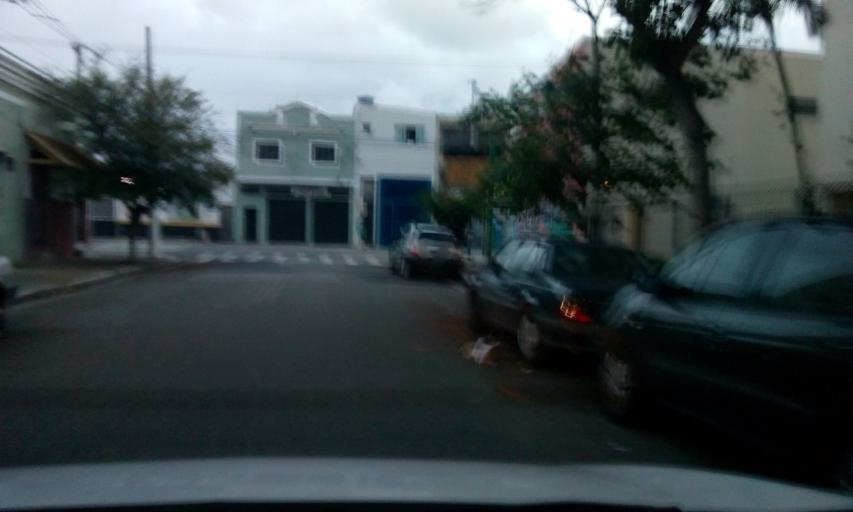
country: BR
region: Sao Paulo
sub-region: Sao Paulo
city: Sao Paulo
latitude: -23.5410
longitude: -46.5871
